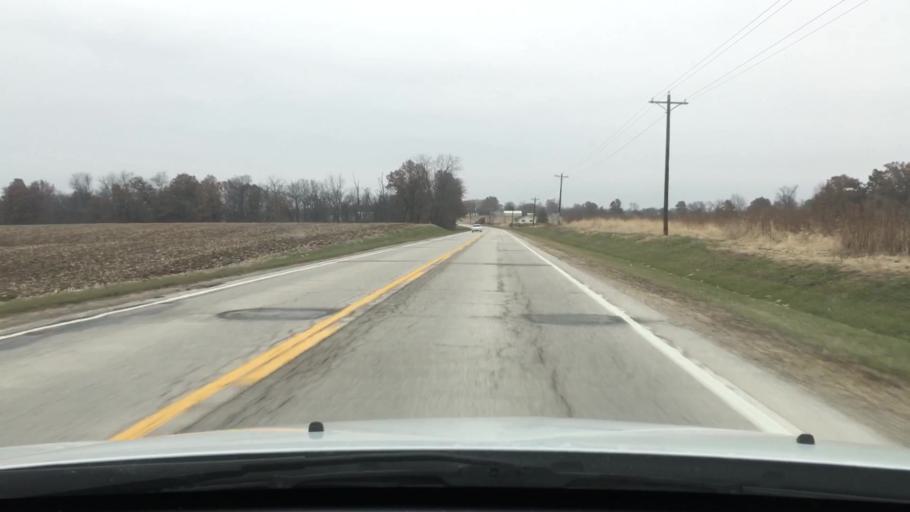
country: US
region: Illinois
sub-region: Pike County
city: Pittsfield
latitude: 39.5659
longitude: -90.9156
